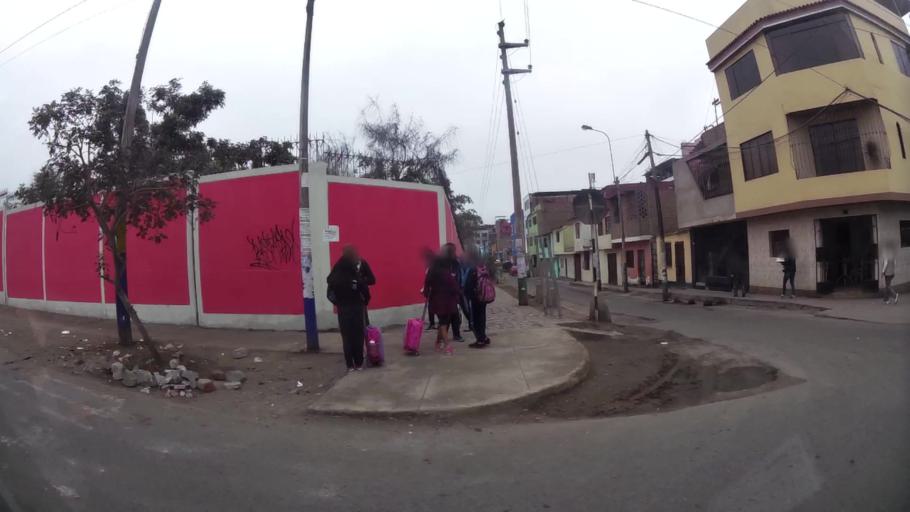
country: PE
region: Lima
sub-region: Lima
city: Surco
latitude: -12.1551
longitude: -76.9549
